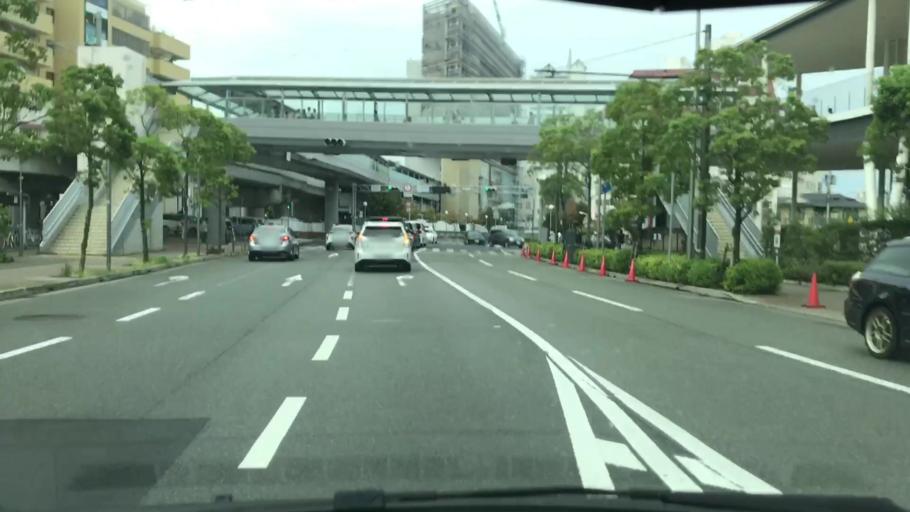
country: JP
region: Hyogo
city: Nishinomiya-hama
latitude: 34.7436
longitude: 135.3579
